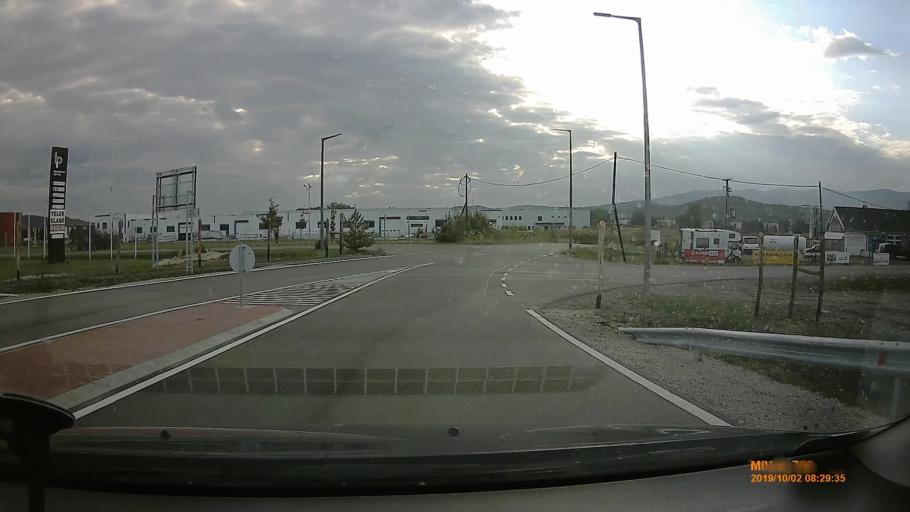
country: HU
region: Nograd
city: Batonyterenye
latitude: 47.9926
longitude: 19.8173
